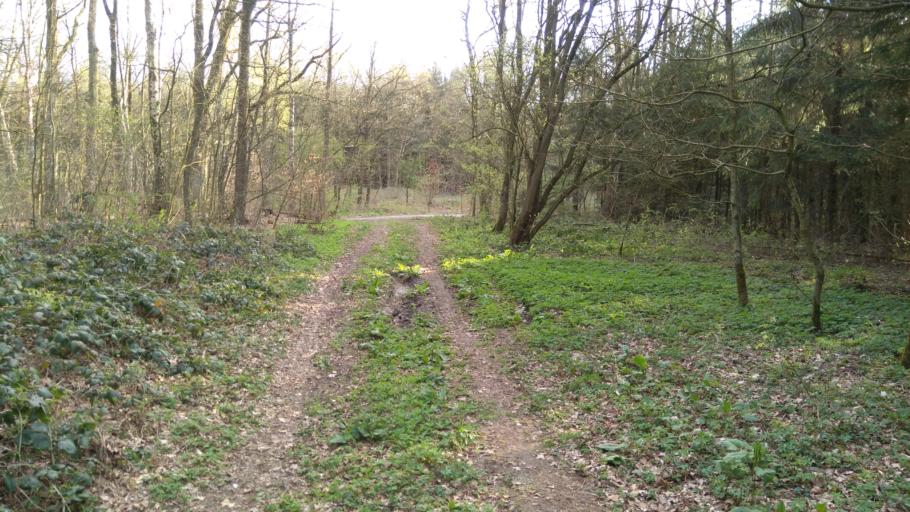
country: DE
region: Lower Saxony
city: Nottensdorf
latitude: 53.4916
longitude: 9.6155
